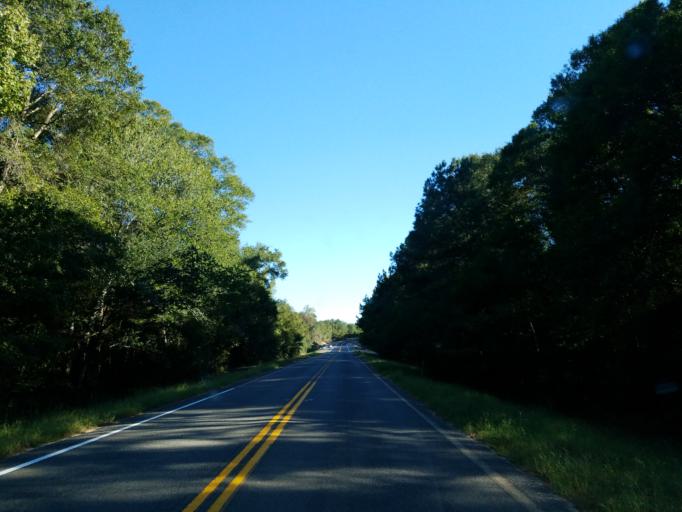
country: US
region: Georgia
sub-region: Dooly County
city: Vienna
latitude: 32.0795
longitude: -83.9584
